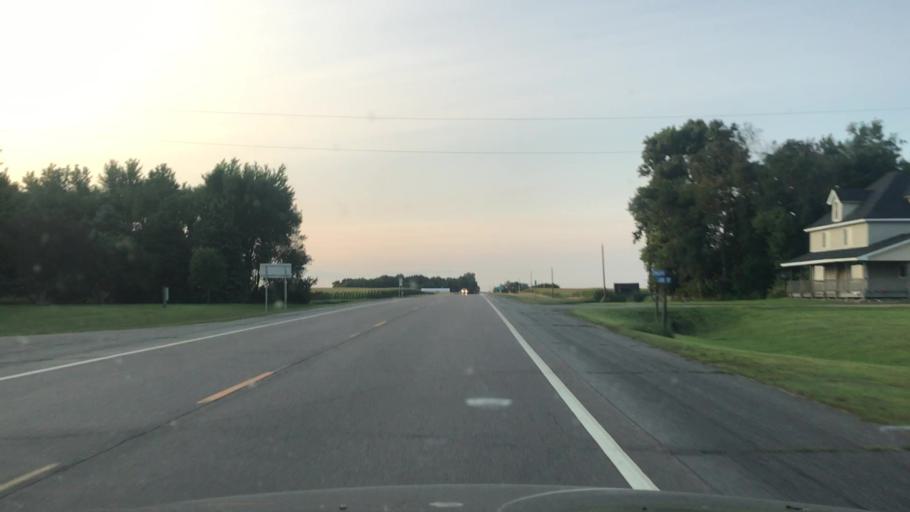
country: US
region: Minnesota
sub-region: Redwood County
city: Redwood Falls
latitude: 44.4073
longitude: -95.1276
